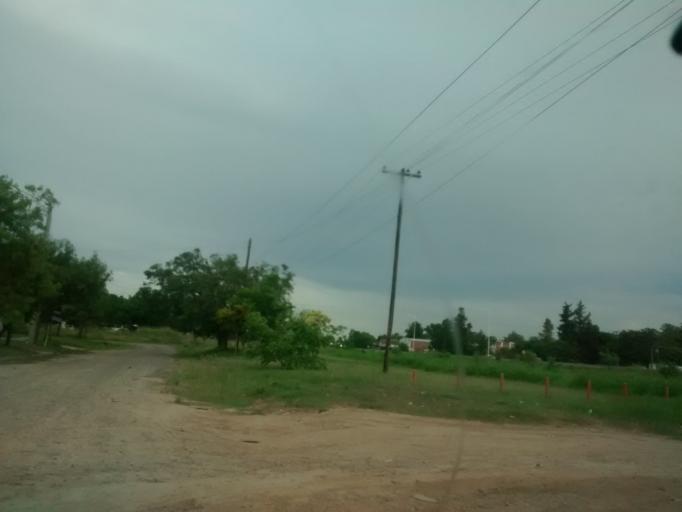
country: AR
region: Chaco
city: Fontana
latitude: -27.4573
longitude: -59.0350
